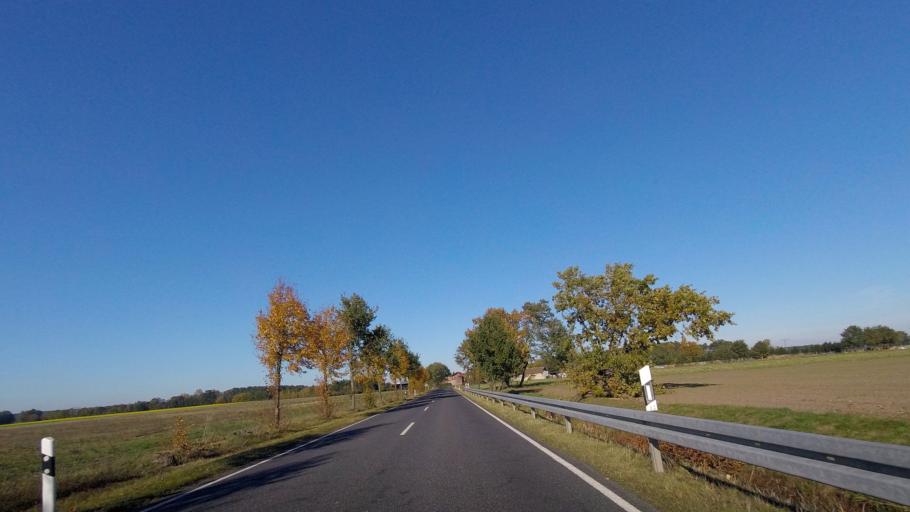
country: DE
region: Saxony-Anhalt
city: Muhlanger
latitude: 51.8615
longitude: 12.7494
